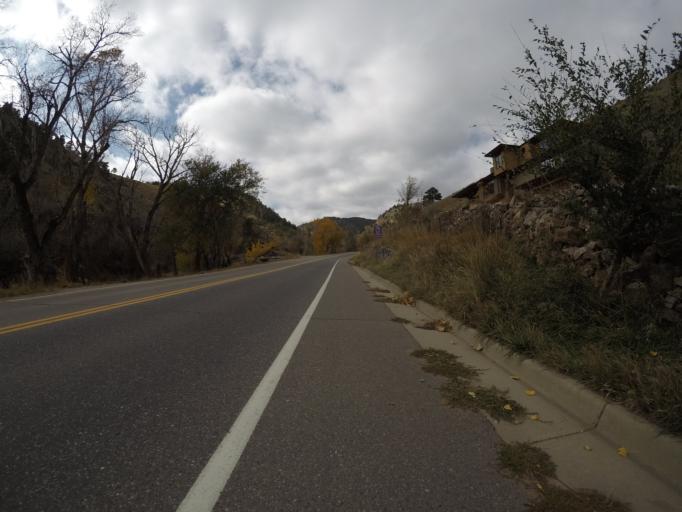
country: US
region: Colorado
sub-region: Boulder County
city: Boulder
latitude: 40.0637
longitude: -105.2978
